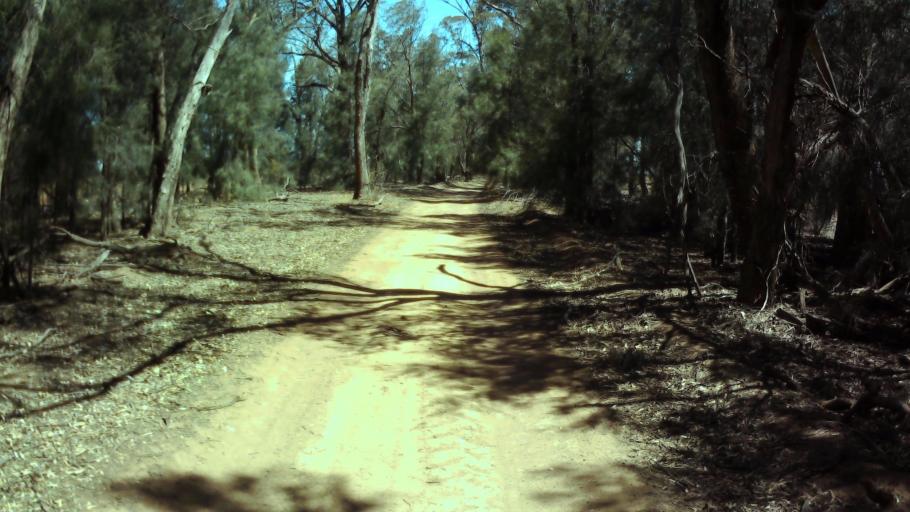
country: AU
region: New South Wales
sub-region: Bland
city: West Wyalong
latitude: -33.9204
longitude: 147.6827
